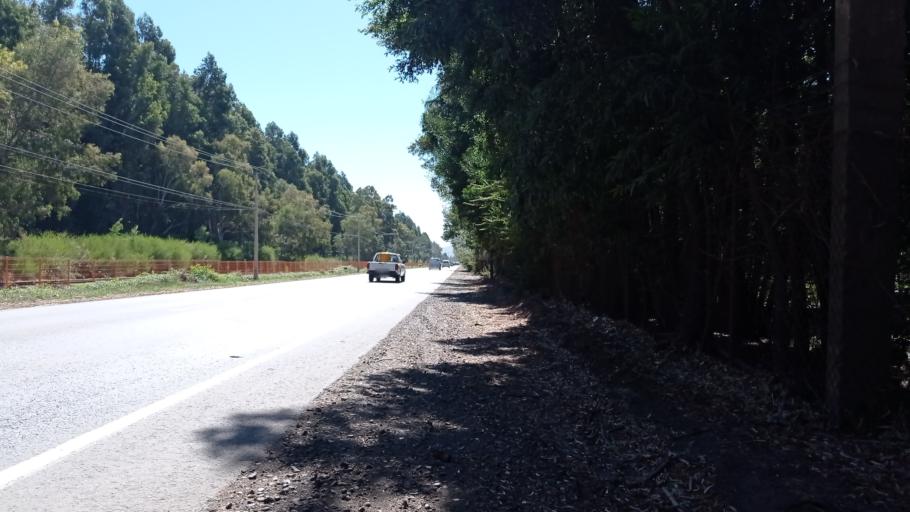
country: CL
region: Biobio
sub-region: Provincia de Biobio
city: Nacimiento
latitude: -37.5292
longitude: -72.6253
